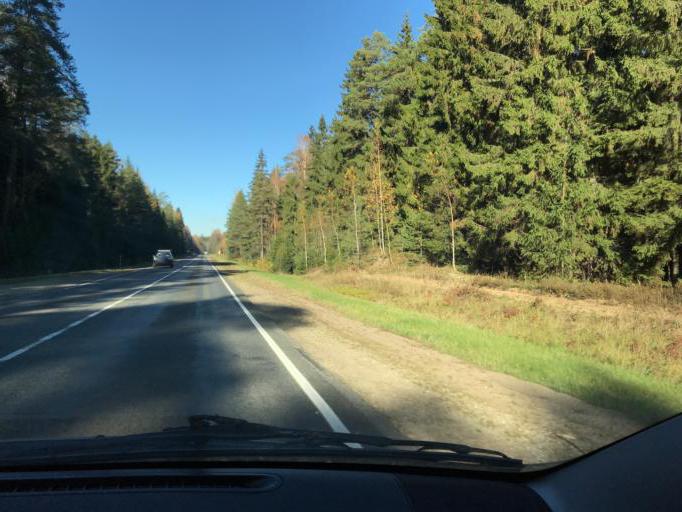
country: BY
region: Vitebsk
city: Polatsk
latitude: 55.4128
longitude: 28.7980
